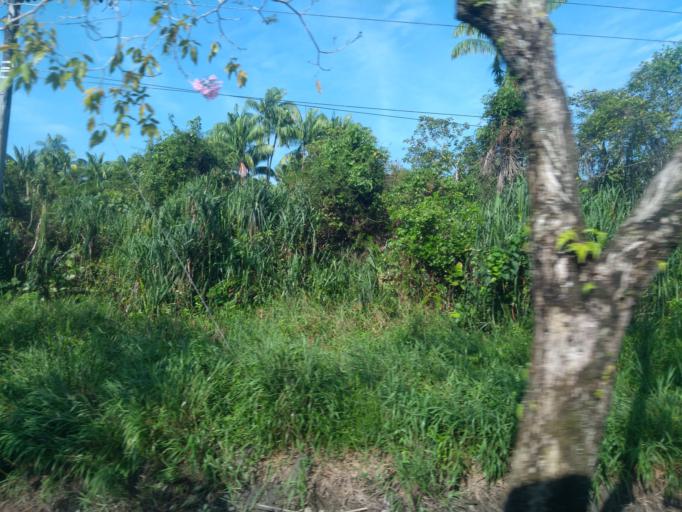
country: MY
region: Sarawak
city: Kuching
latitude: 1.6532
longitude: 110.4443
